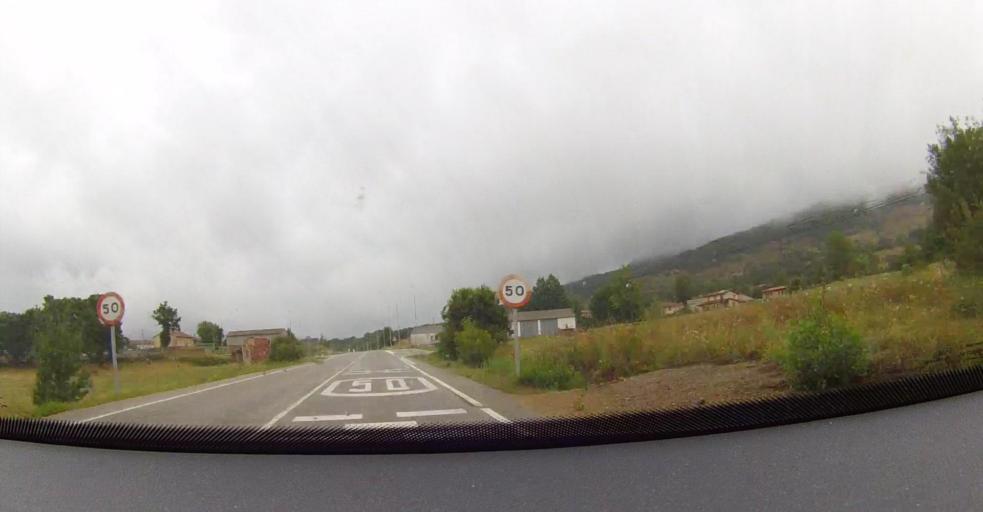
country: ES
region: Castille and Leon
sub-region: Provincia de Leon
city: Bonar
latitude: 42.8483
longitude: -5.2732
